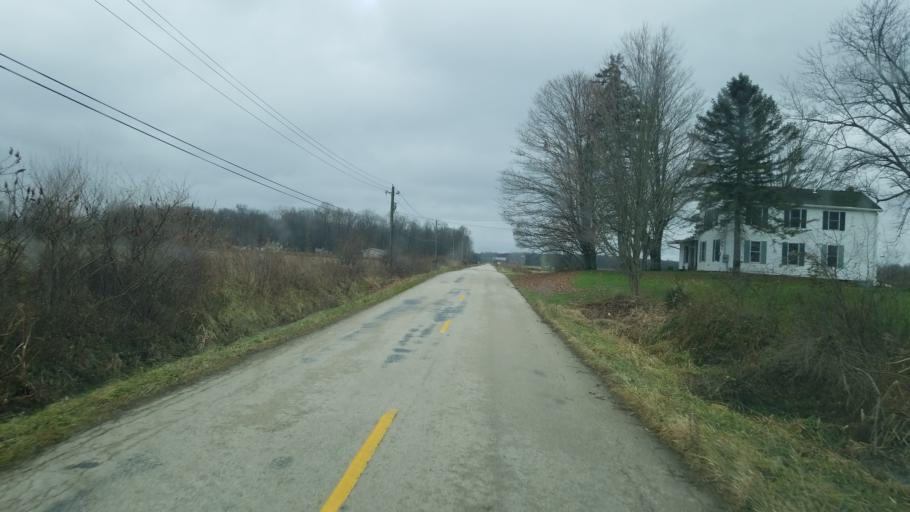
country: US
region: Ohio
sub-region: Ashtabula County
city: Roaming Shores
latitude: 41.6160
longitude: -80.8259
